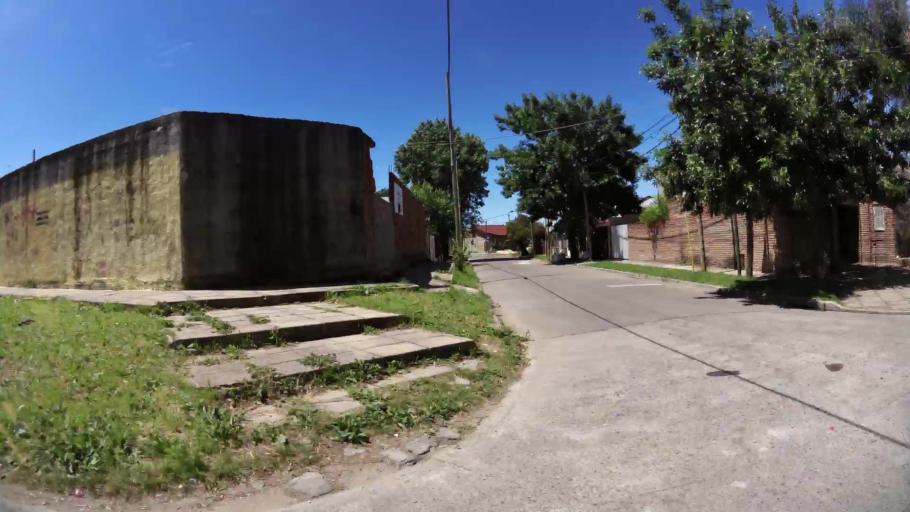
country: AR
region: Buenos Aires
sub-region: Partido de General San Martin
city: General San Martin
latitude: -34.5166
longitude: -58.5584
